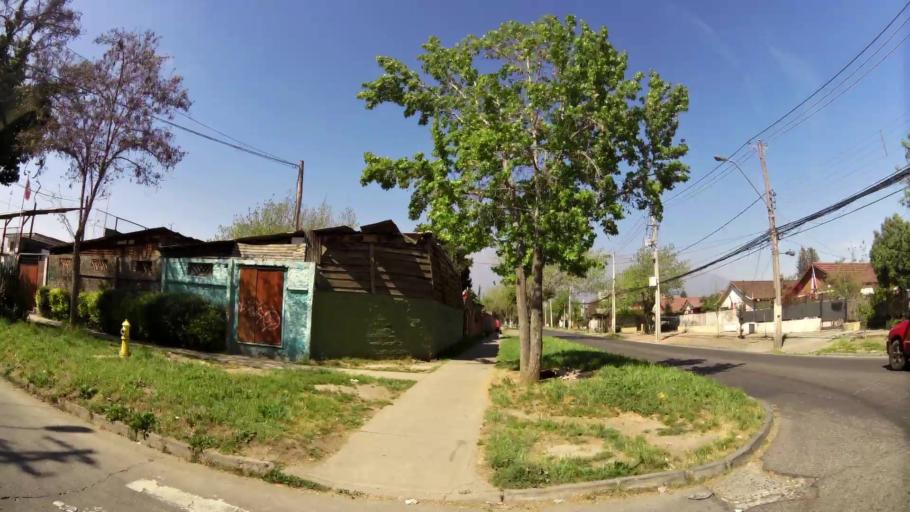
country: CL
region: Santiago Metropolitan
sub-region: Provincia de Santiago
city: Villa Presidente Frei, Nunoa, Santiago, Chile
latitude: -33.4865
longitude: -70.5885
